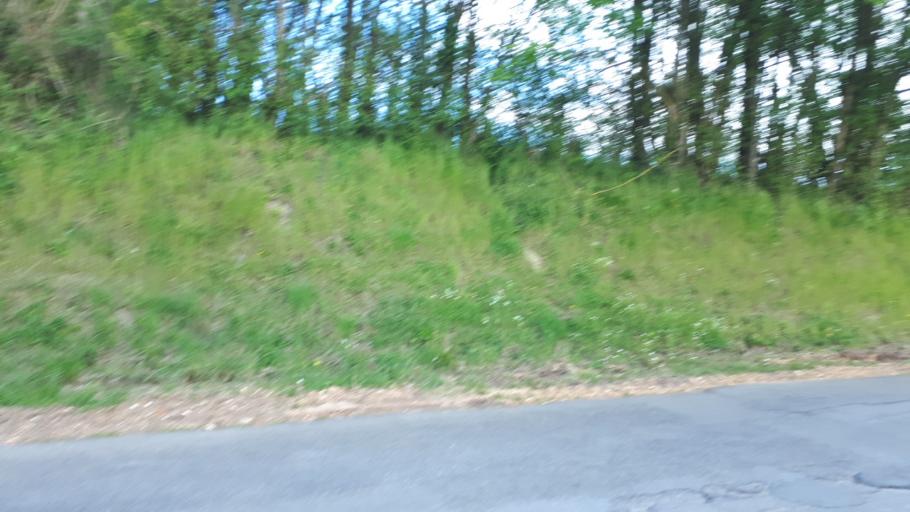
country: FR
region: Centre
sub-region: Departement du Loir-et-Cher
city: Aze
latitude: 47.8485
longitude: 0.9999
